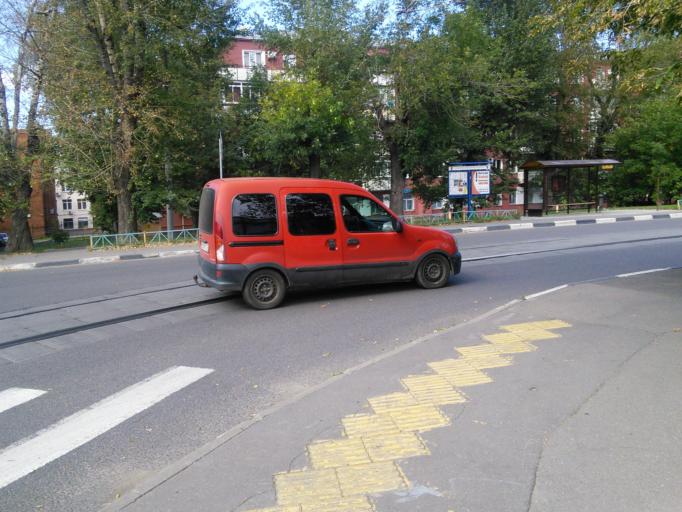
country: RU
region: Moscow
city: Lefortovo
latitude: 55.7852
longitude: 37.7144
